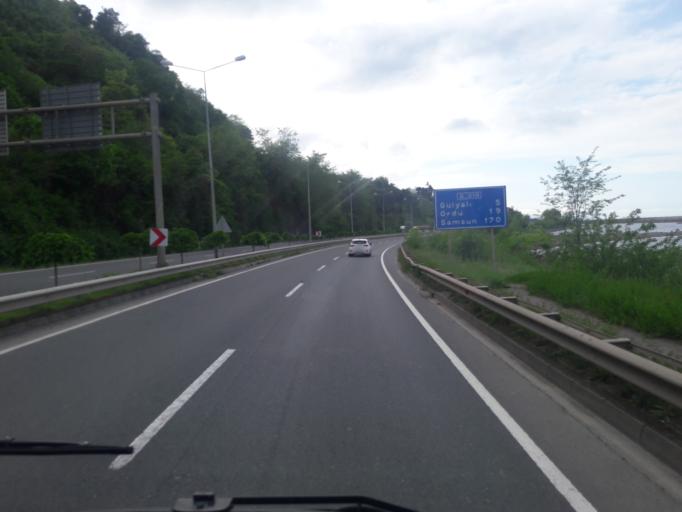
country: TR
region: Giresun
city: Piraziz
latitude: 40.9579
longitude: 38.1119
